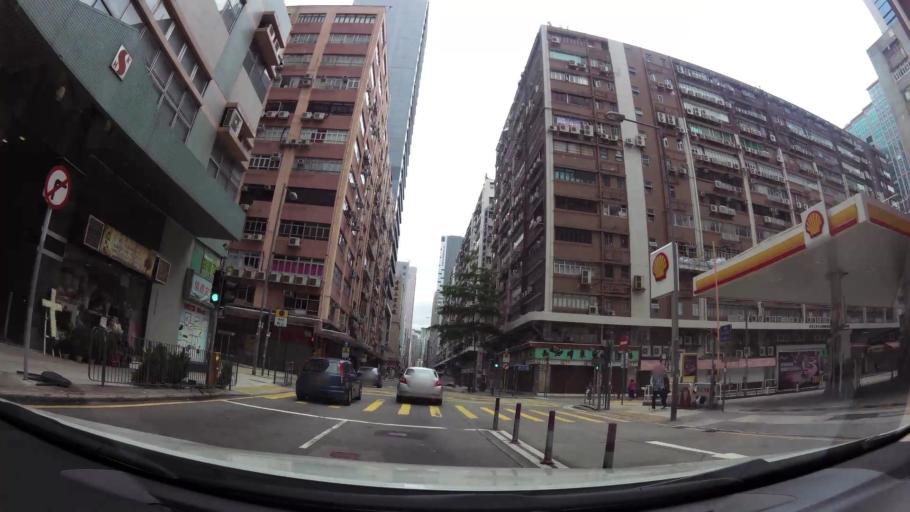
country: HK
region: Sham Shui Po
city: Sham Shui Po
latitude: 22.3376
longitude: 114.1463
